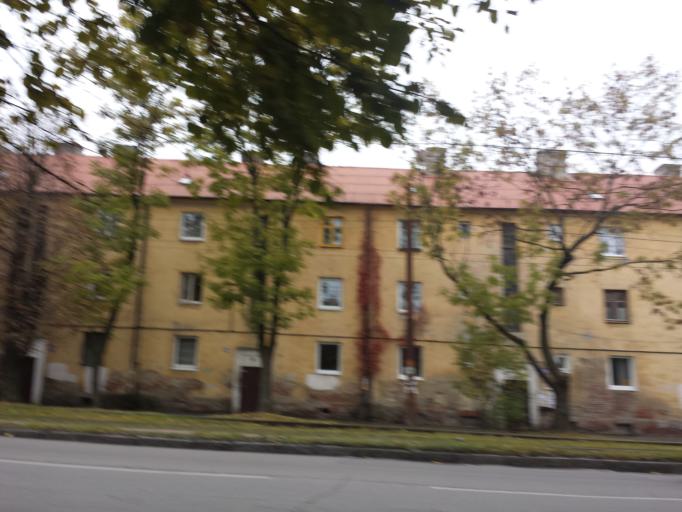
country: RU
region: Kaliningrad
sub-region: Gorod Kaliningrad
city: Kaliningrad
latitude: 54.6905
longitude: 20.5236
